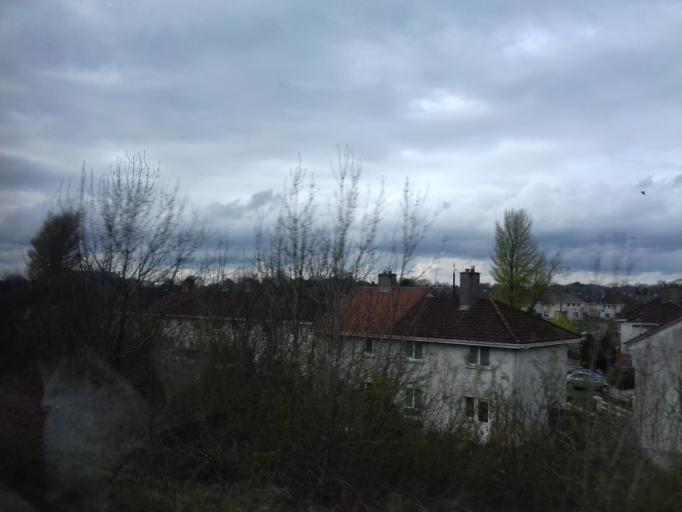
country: IE
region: Leinster
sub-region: An Longfort
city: Longford
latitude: 53.7263
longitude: -7.7865
